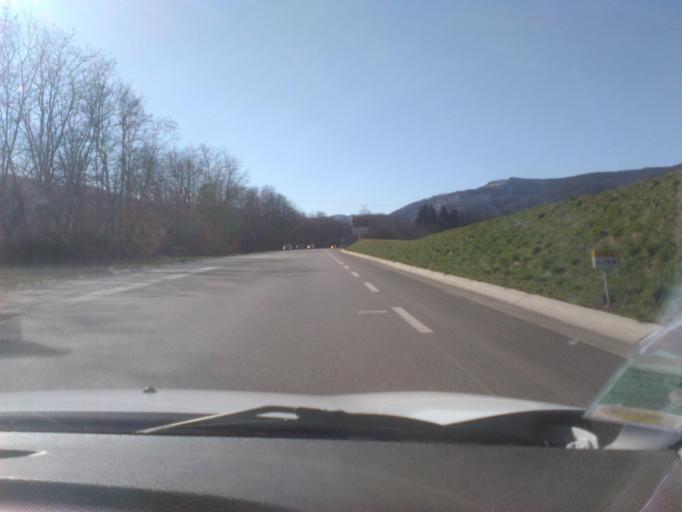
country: FR
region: Alsace
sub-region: Departement du Bas-Rhin
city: Wisches
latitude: 48.5029
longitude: 7.2732
